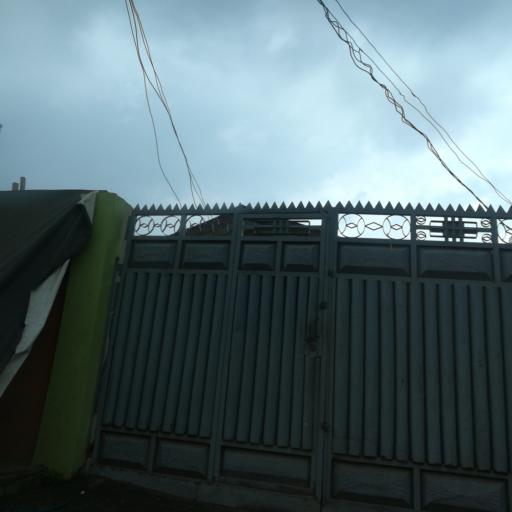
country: NG
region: Lagos
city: Agege
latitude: 6.5959
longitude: 3.2975
